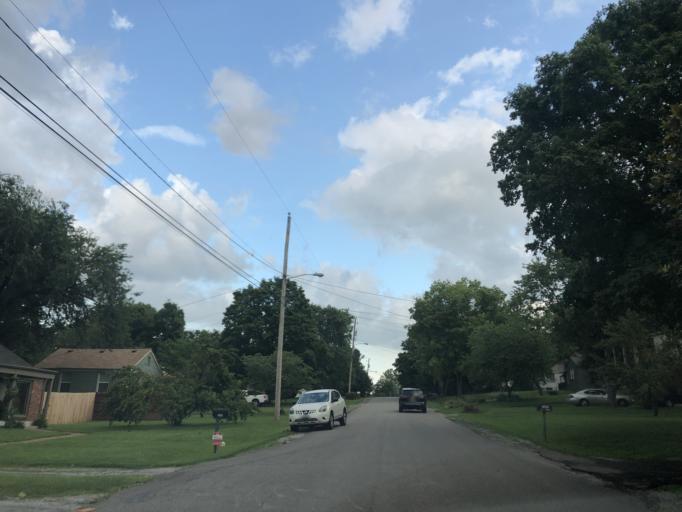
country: US
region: Tennessee
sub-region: Davidson County
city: Lakewood
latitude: 36.1792
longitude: -86.6870
